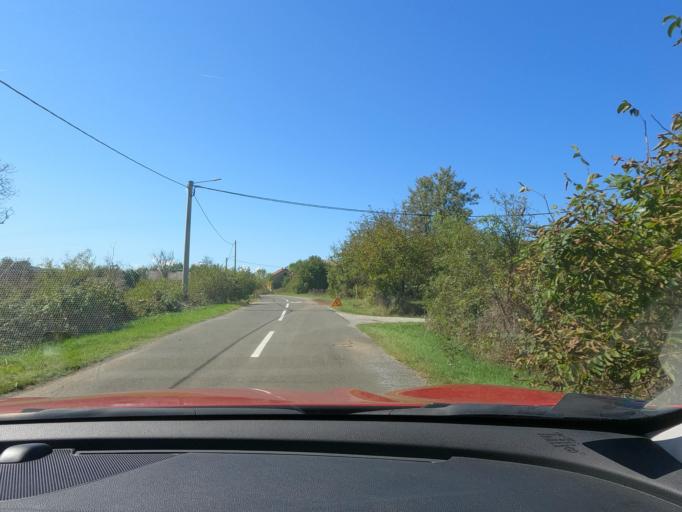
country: HR
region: Sisacko-Moslavacka
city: Petrinja
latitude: 45.3311
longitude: 16.2396
